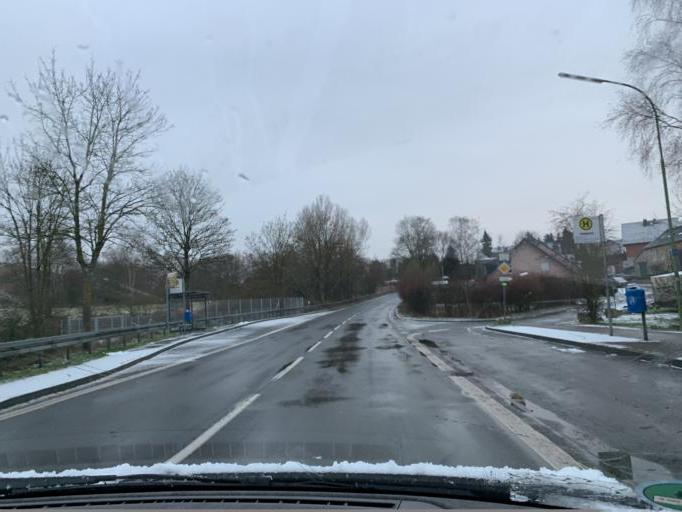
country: DE
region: North Rhine-Westphalia
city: Stolberg
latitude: 50.7401
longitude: 6.2431
